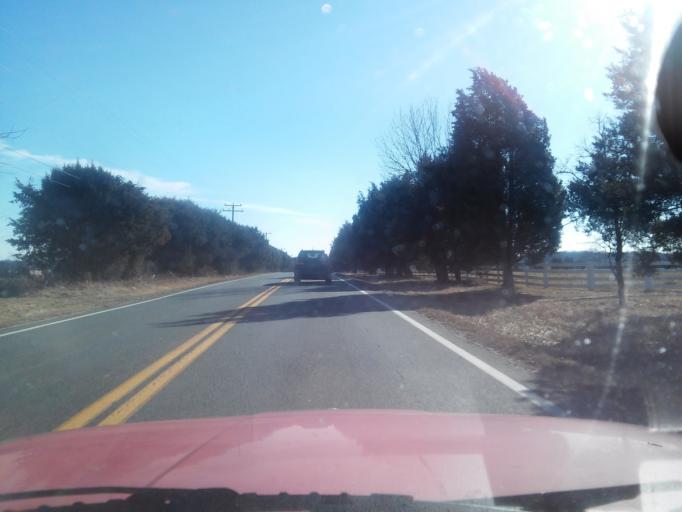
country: US
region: Virginia
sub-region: Orange County
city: Gordonsville
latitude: 38.0281
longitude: -78.1903
